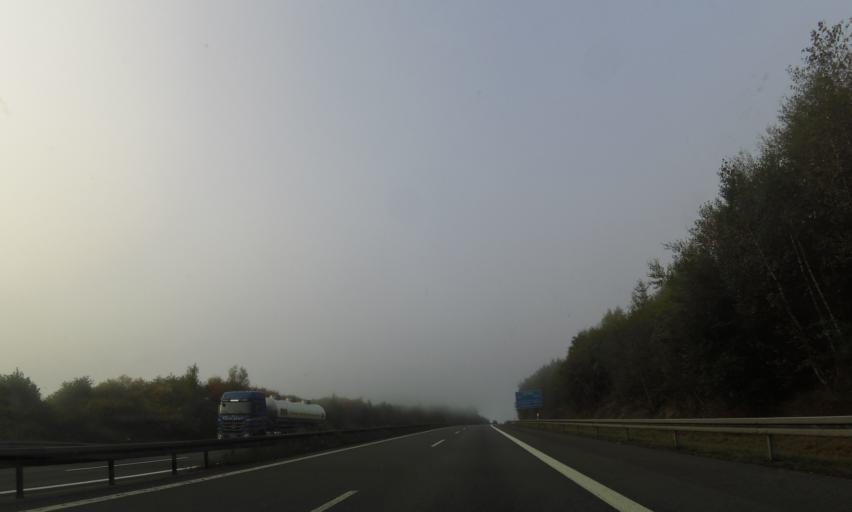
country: DE
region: Saxony
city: Weischlitz
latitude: 50.4318
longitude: 12.0773
